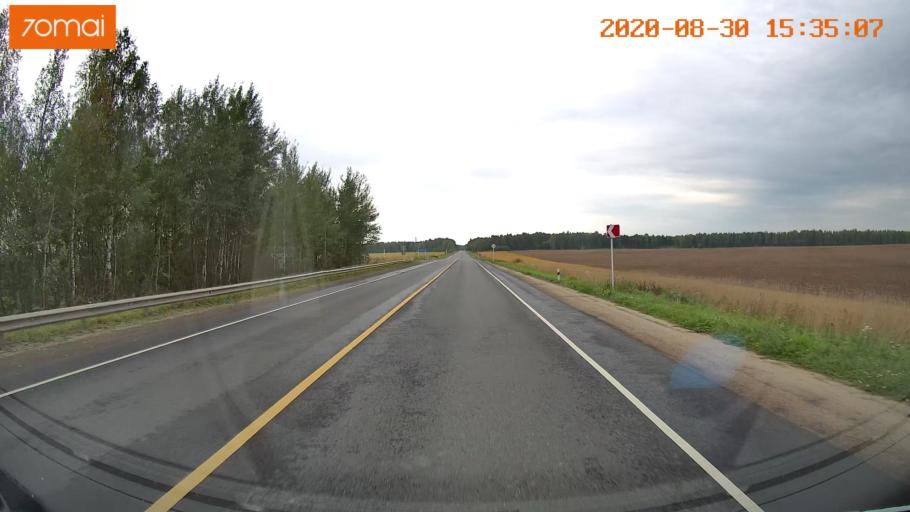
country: RU
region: Ivanovo
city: Kaminskiy
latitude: 57.0656
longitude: 41.4111
